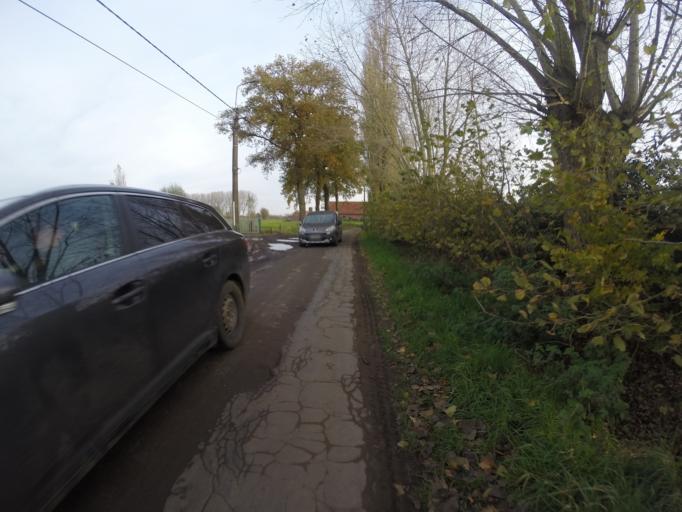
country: BE
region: Flanders
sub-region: Provincie Oost-Vlaanderen
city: Nevele
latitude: 51.0554
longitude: 3.4971
